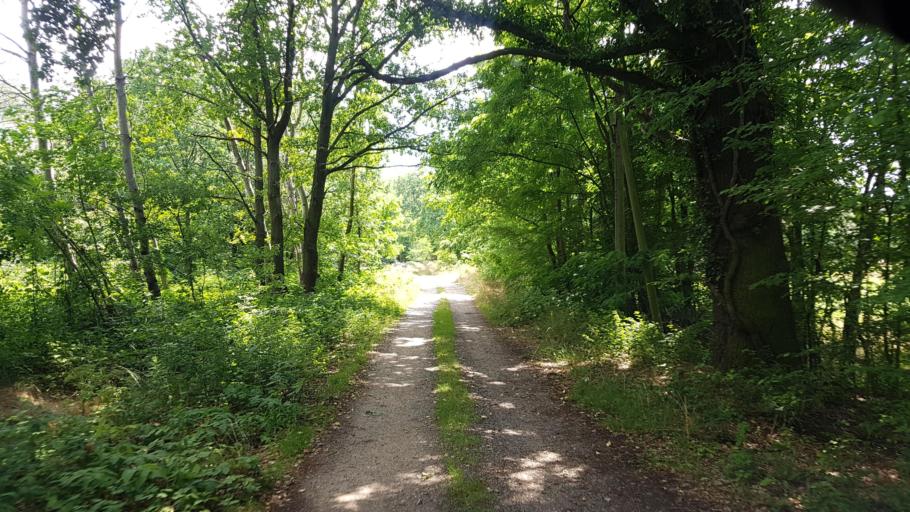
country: DE
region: Brandenburg
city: Crinitz
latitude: 51.7564
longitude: 13.8149
